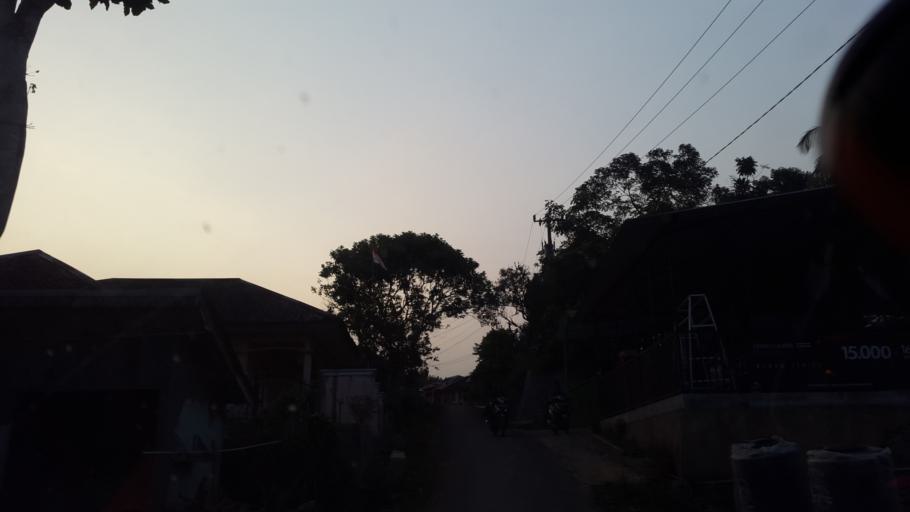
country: ID
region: West Java
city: Sukamaju
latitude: -7.1624
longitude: 106.9385
